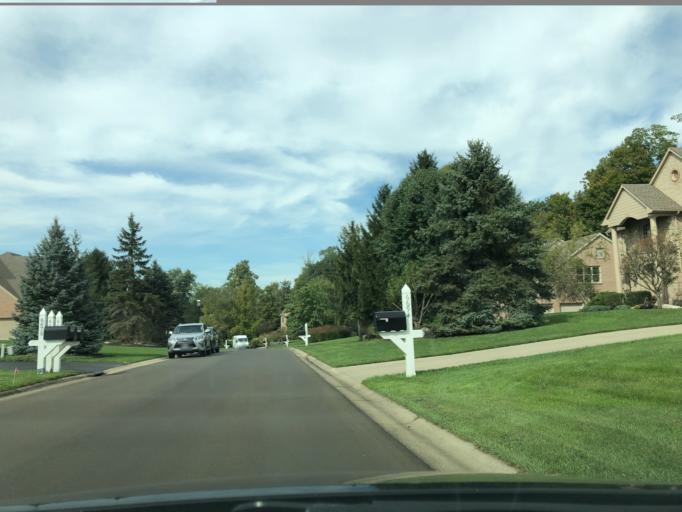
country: US
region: Ohio
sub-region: Hamilton County
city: Loveland
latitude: 39.2477
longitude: -84.2611
